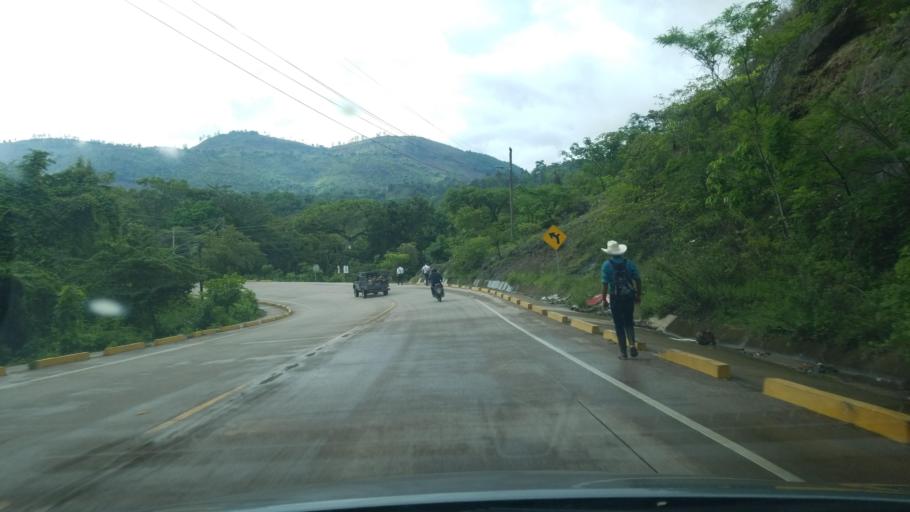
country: HN
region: Copan
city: Copan
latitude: 14.8415
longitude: -89.1635
